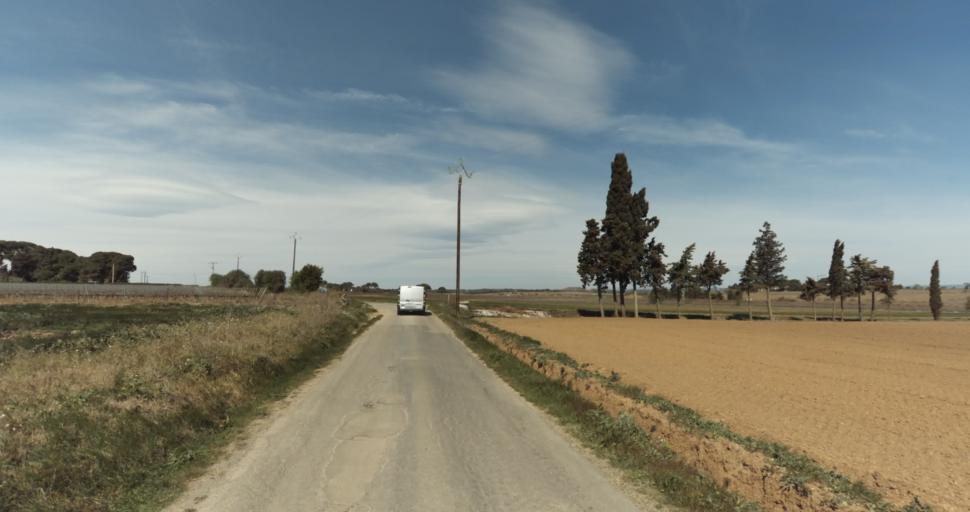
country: FR
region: Languedoc-Roussillon
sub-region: Departement de l'Herault
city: Marseillan
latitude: 43.3889
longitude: 3.5416
